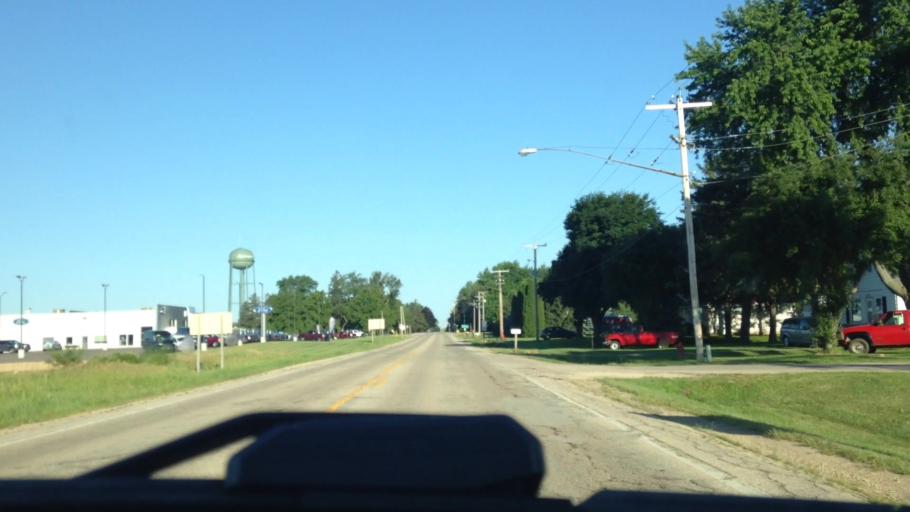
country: US
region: Wisconsin
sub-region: Columbia County
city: Poynette
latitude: 43.3375
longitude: -89.3692
